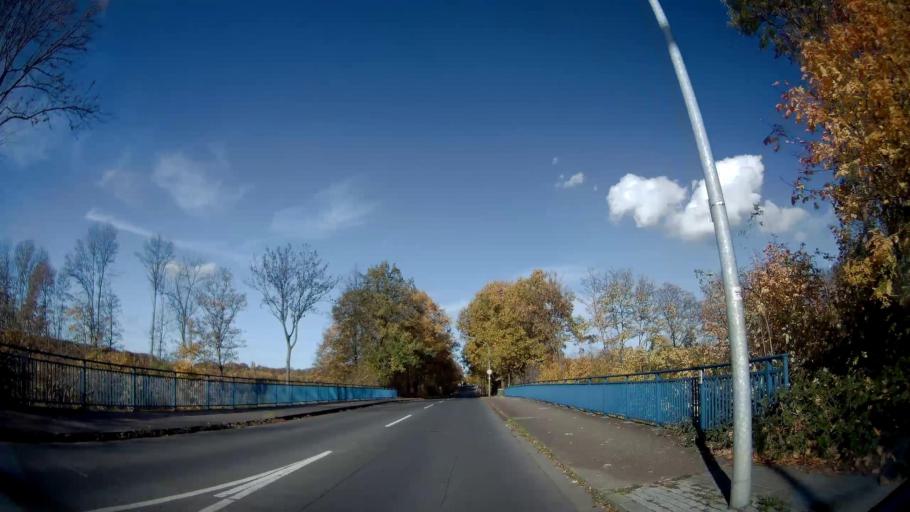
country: DE
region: North Rhine-Westphalia
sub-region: Regierungsbezirk Munster
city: Gladbeck
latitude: 51.5746
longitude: 7.0198
